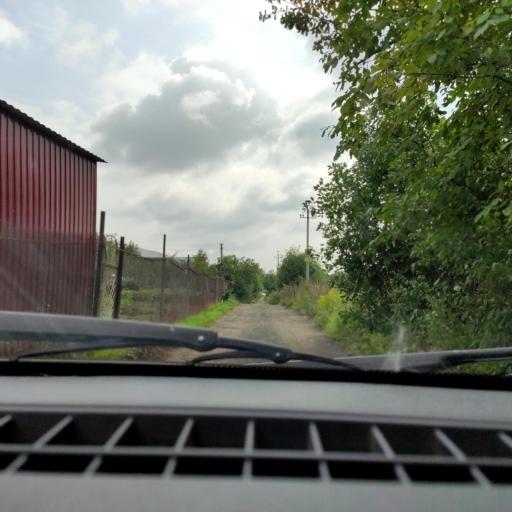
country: RU
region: Bashkortostan
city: Mikhaylovka
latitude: 54.8306
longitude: 55.8318
